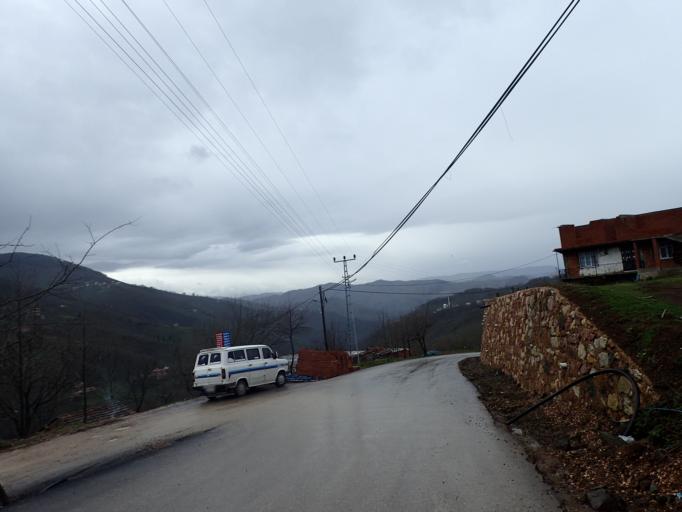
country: TR
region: Ordu
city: Camas
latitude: 40.8783
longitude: 37.5086
